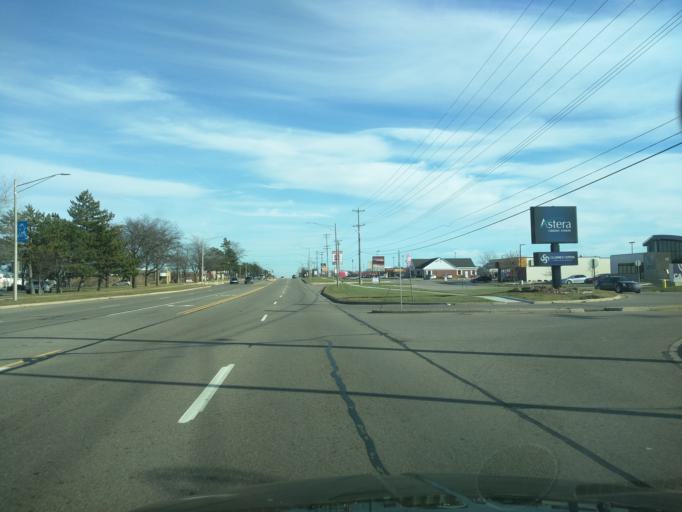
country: US
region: Michigan
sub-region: Eaton County
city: Waverly
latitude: 42.7410
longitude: -84.6300
